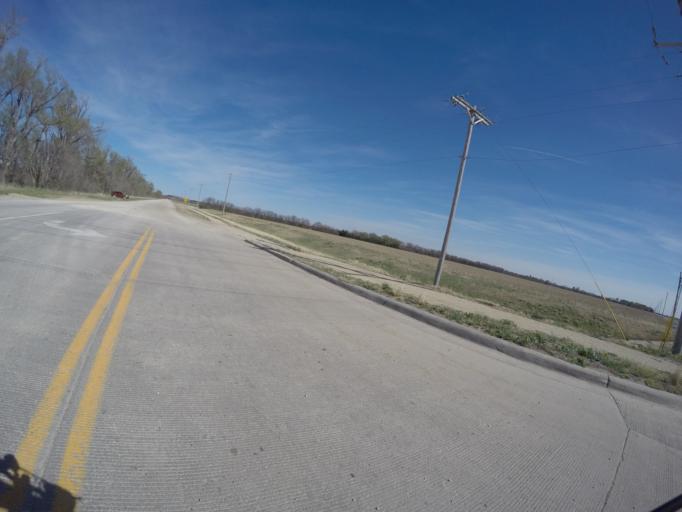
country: US
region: Kansas
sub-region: Saline County
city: Salina
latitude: 38.7834
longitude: -97.5942
